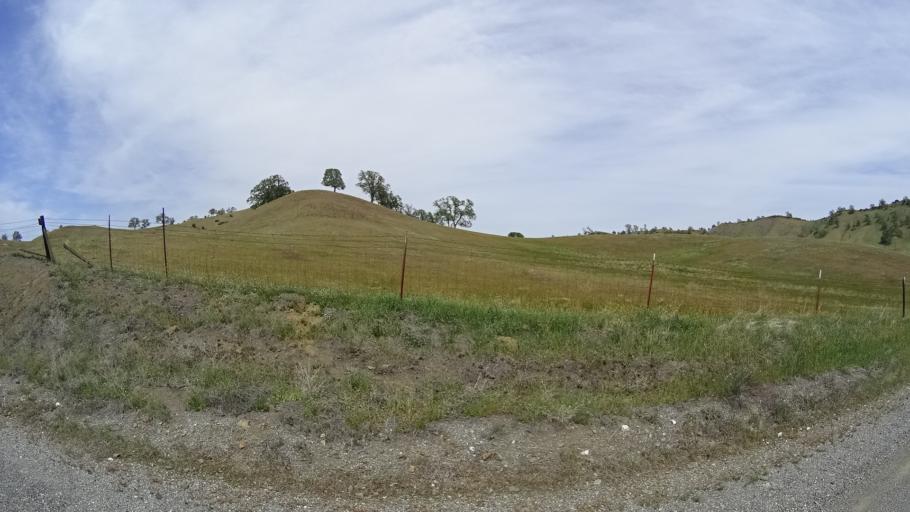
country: US
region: California
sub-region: Glenn County
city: Willows
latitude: 39.6163
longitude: -122.5905
